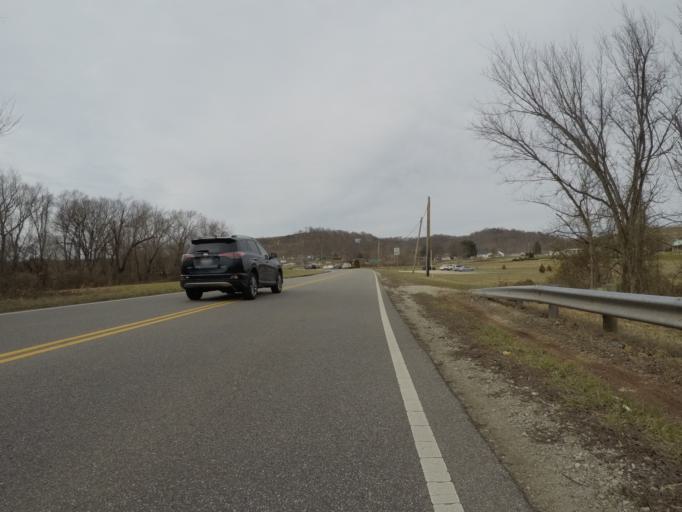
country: US
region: West Virginia
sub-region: Cabell County
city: Pea Ridge
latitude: 38.4421
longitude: -82.3746
